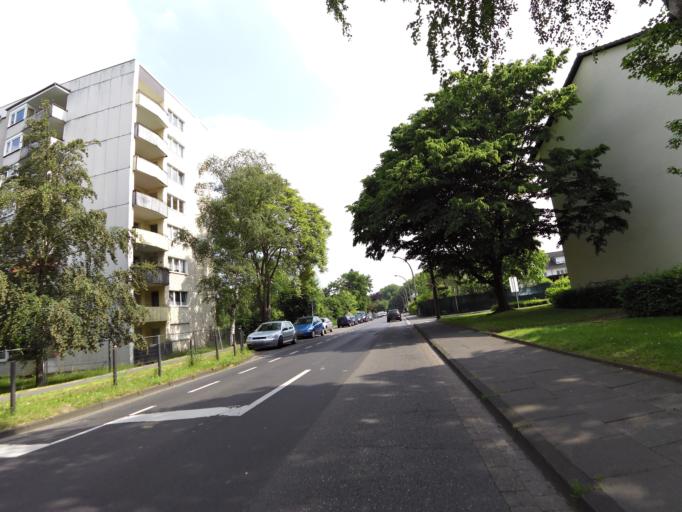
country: DE
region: North Rhine-Westphalia
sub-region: Regierungsbezirk Koln
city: Bonn
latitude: 50.7151
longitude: 7.0591
